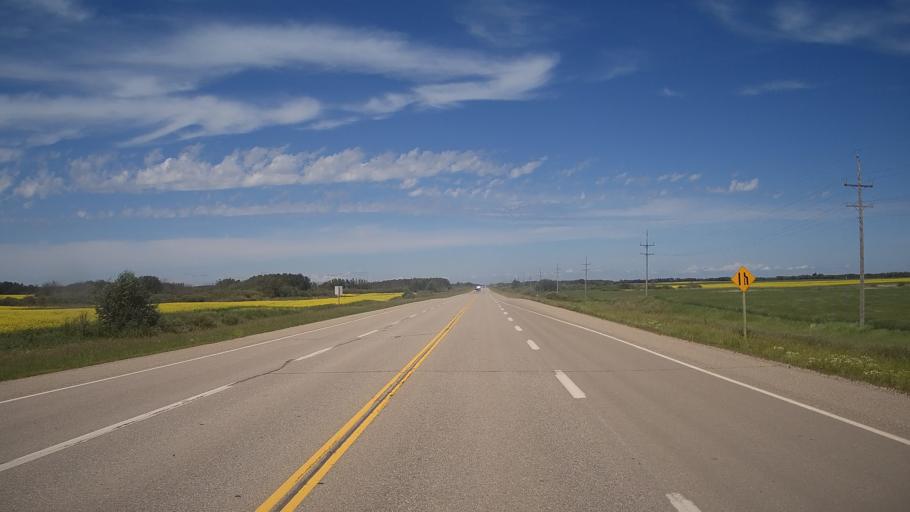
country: CA
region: Saskatchewan
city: Langenburg
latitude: 50.6388
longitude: -101.2760
